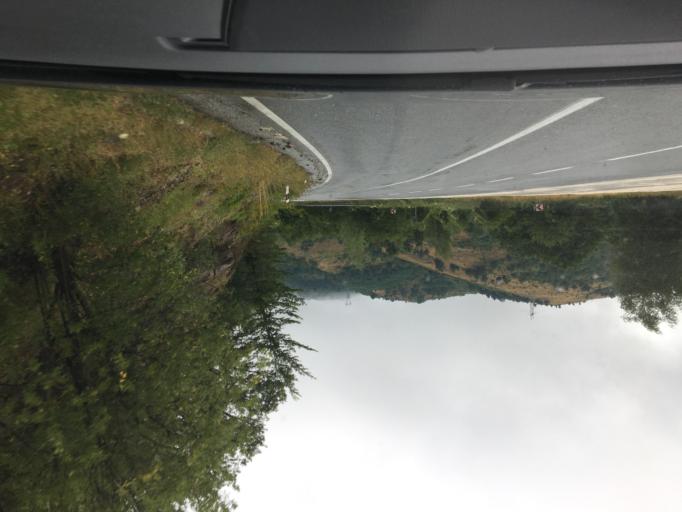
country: MK
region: Kriva Palanka
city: Kriva Palanka
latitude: 42.2191
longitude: 22.4446
